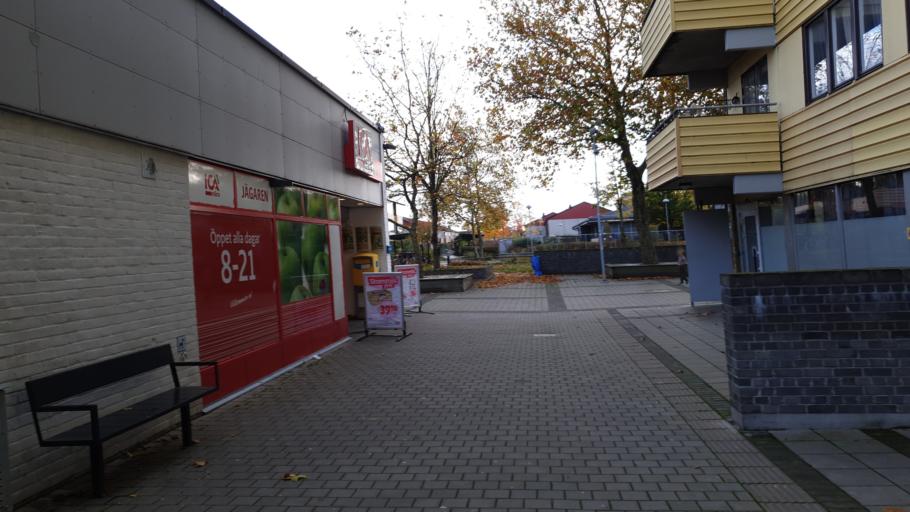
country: SE
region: Skane
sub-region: Lunds Kommun
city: Lund
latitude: 55.7278
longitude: 13.1748
